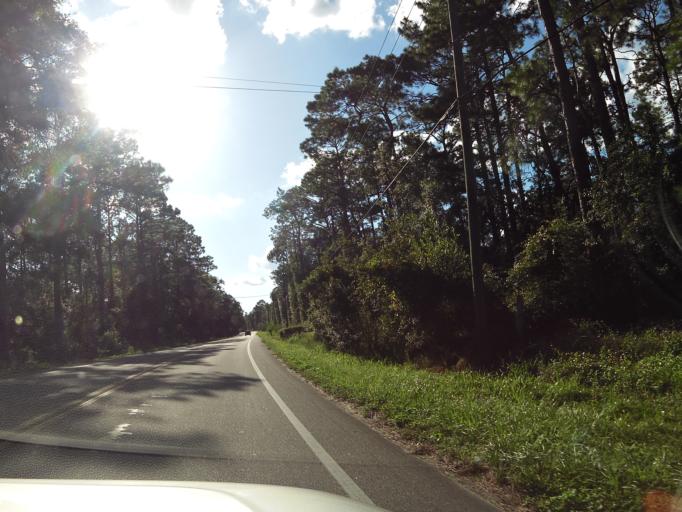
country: US
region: Florida
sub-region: Wakulla County
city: Crawfordville
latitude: 30.0717
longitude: -84.4410
